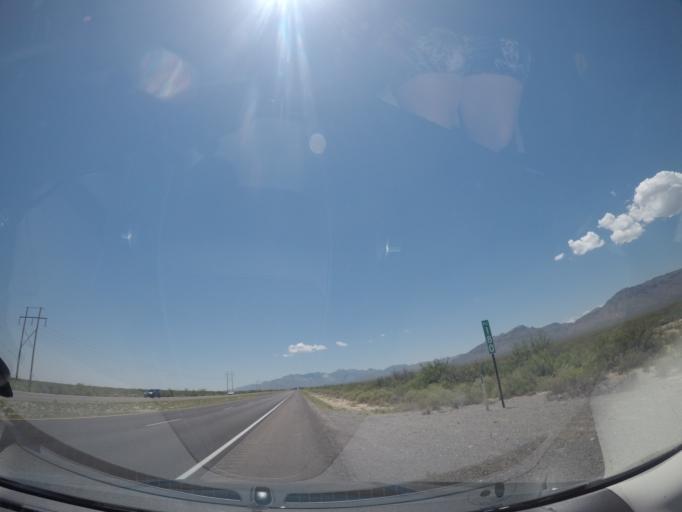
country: US
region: New Mexico
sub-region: Dona Ana County
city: White Sands
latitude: 32.5420
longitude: -106.3570
